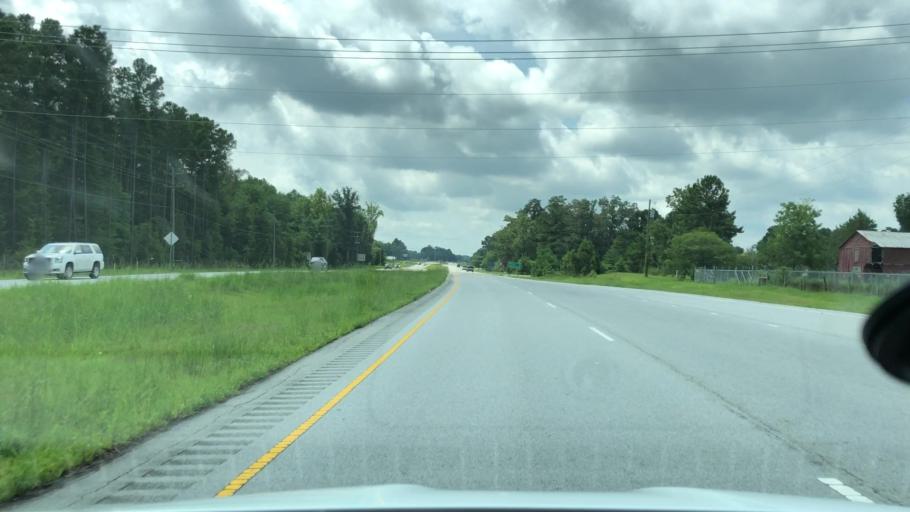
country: US
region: North Carolina
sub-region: Beaufort County
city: Washington
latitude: 35.4988
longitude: -77.1042
